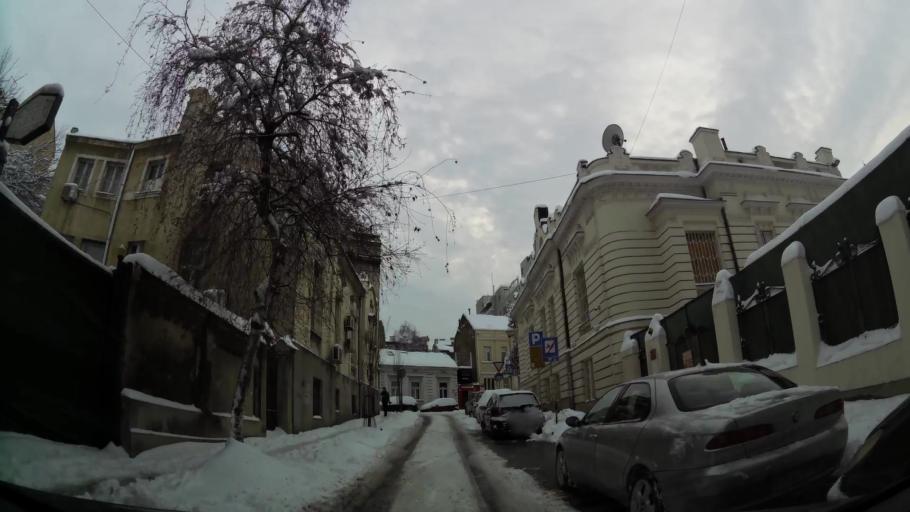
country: RS
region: Central Serbia
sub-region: Belgrade
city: Stari Grad
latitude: 44.8156
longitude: 20.4679
